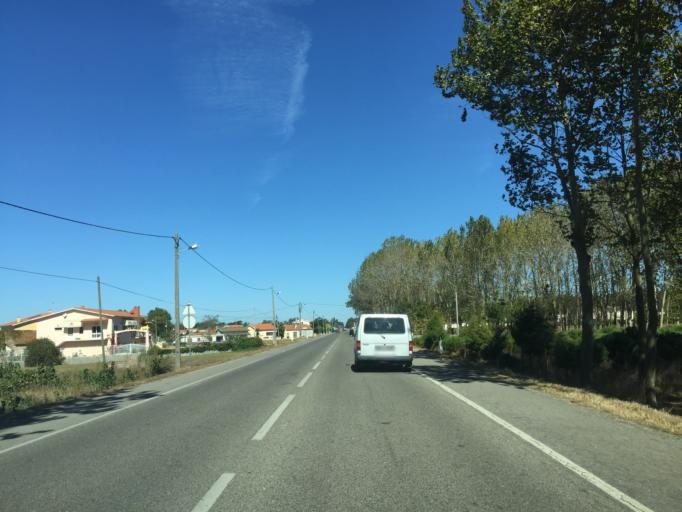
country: PT
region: Coimbra
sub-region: Figueira da Foz
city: Alhadas
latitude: 40.2771
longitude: -8.7734
